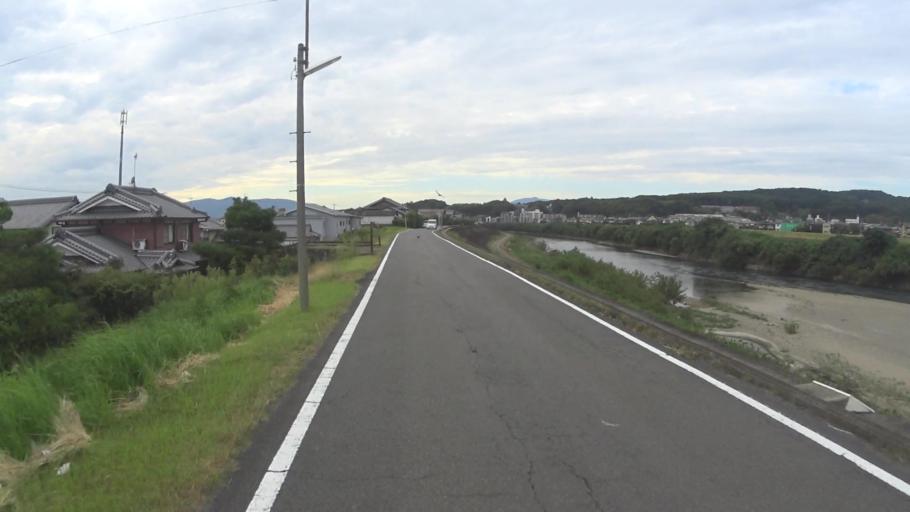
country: JP
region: Kyoto
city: Uji
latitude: 34.9237
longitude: 135.7834
